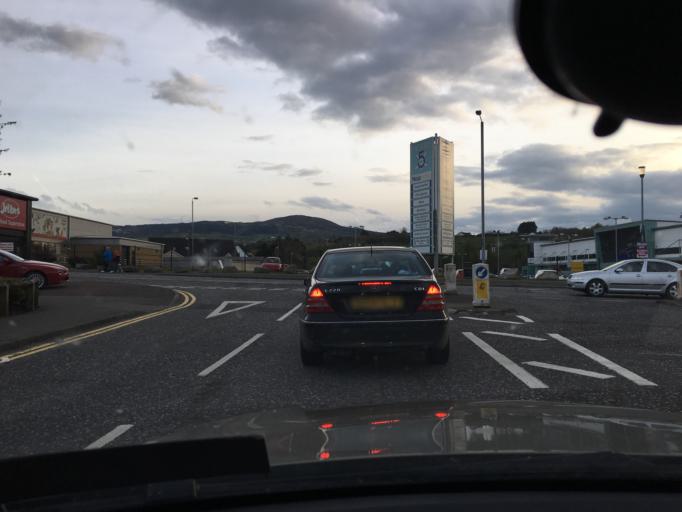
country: GB
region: Northern Ireland
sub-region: Newry and Mourne District
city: Newry
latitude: 54.1912
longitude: -6.3502
